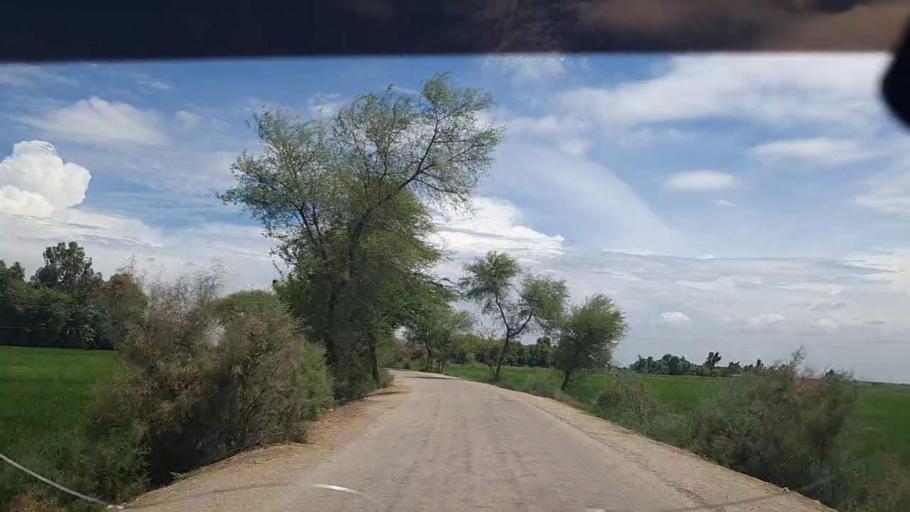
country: PK
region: Sindh
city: Ghauspur
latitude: 28.1564
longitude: 69.0034
